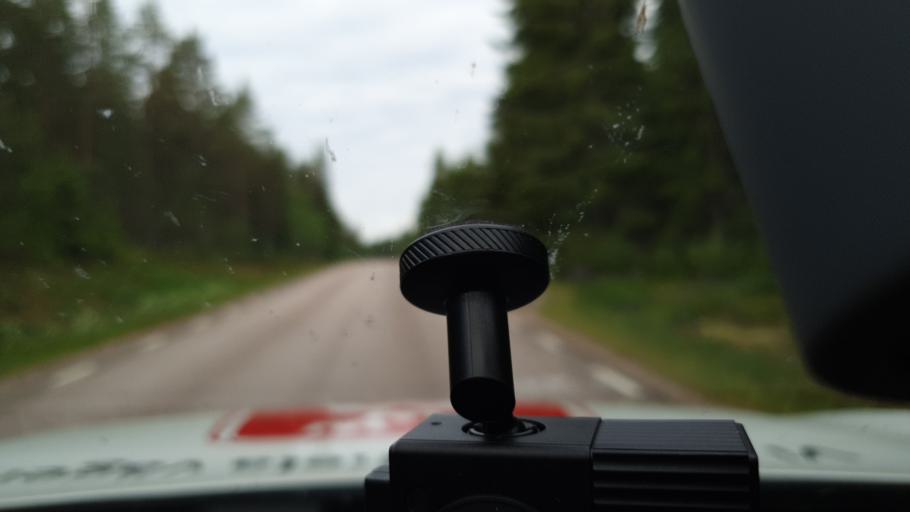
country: SE
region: Vaermland
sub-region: Torsby Kommun
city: Torsby
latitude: 60.1127
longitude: 12.9228
